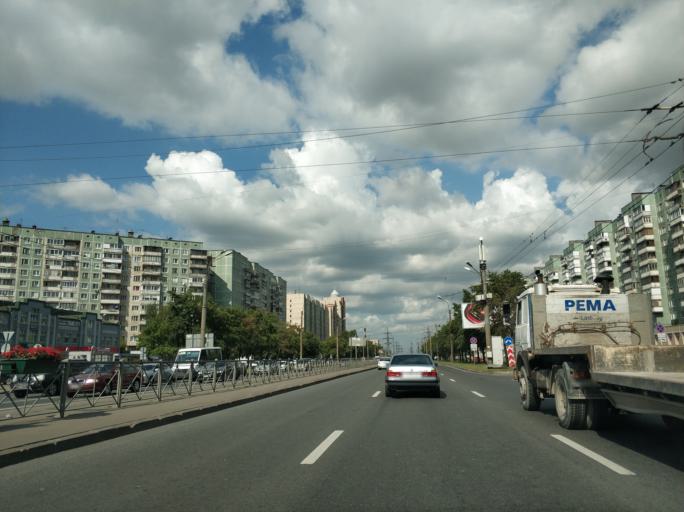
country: RU
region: St.-Petersburg
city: Krasnogvargeisky
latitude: 59.9517
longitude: 30.4714
